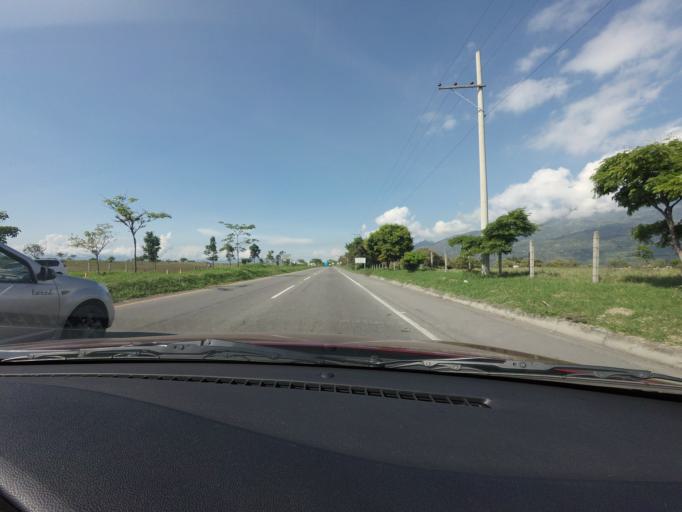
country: CO
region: Cundinamarca
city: Fusagasuga
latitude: 4.3426
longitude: -74.4060
